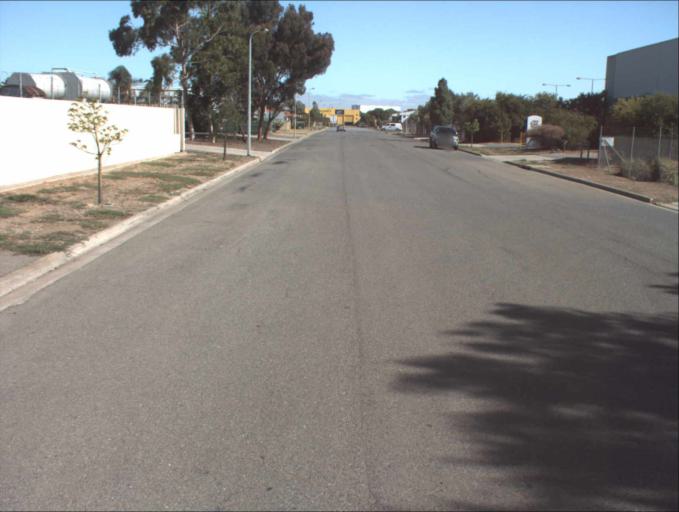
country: AU
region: South Australia
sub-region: Port Adelaide Enfield
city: Blair Athol
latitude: -34.8433
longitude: 138.5677
